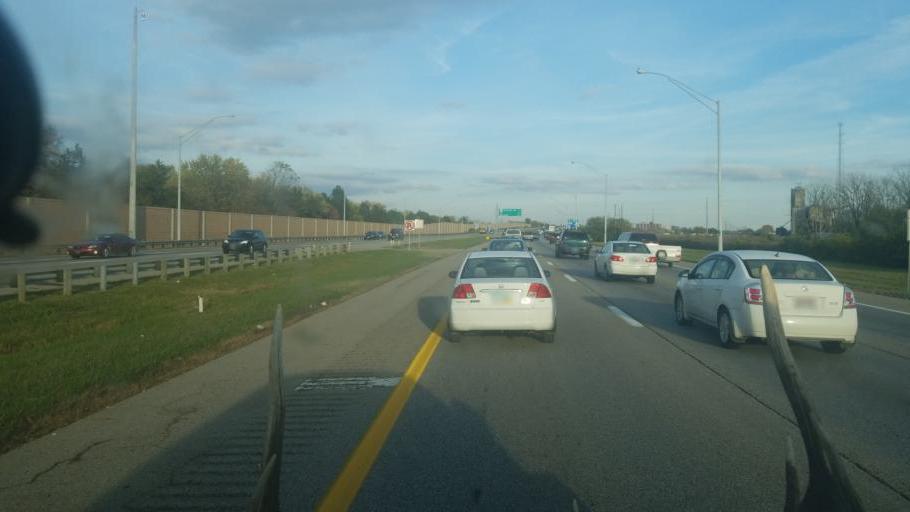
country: US
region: Ohio
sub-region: Franklin County
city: Whitehall
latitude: 39.9346
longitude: -82.8953
